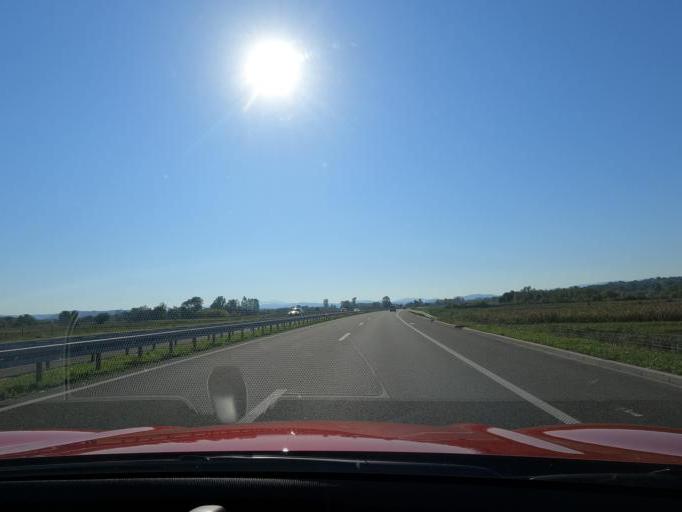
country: RS
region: Central Serbia
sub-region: Kolubarski Okrug
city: Ljig
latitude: 44.3052
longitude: 20.2293
